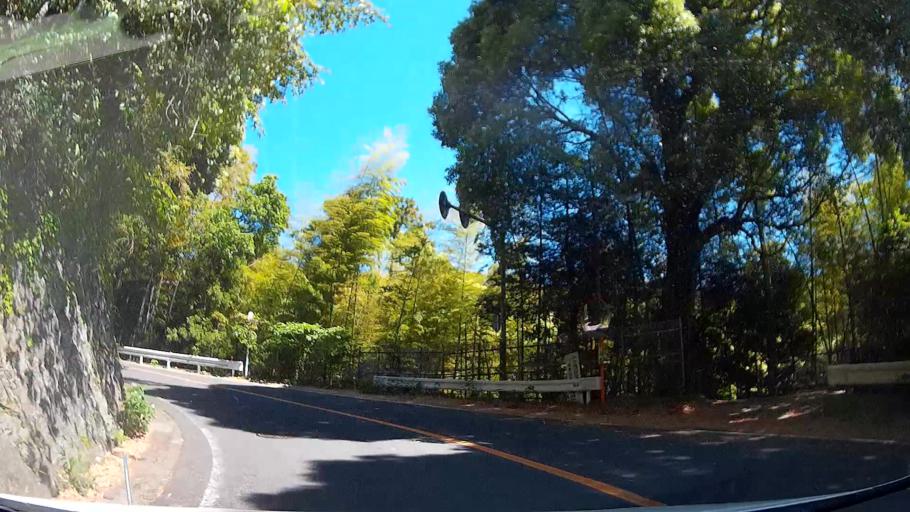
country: JP
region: Shizuoka
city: Atami
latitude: 35.1028
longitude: 139.0653
